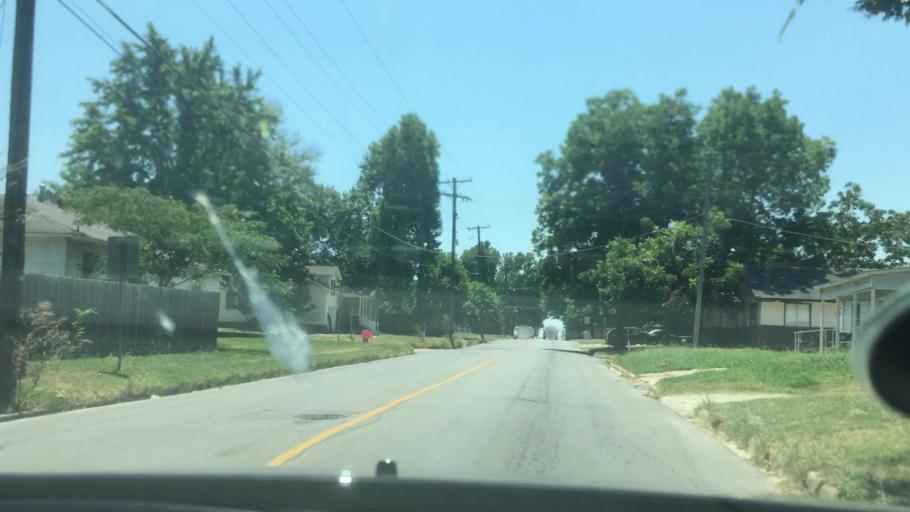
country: US
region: Oklahoma
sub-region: Pontotoc County
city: Ada
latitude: 34.7799
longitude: -96.6634
